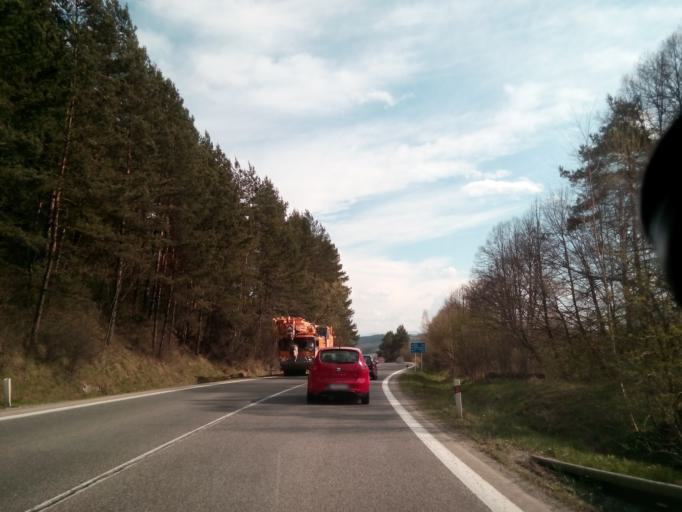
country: SK
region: Presovsky
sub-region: Okres Presov
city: Levoca
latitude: 49.0270
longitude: 20.6188
